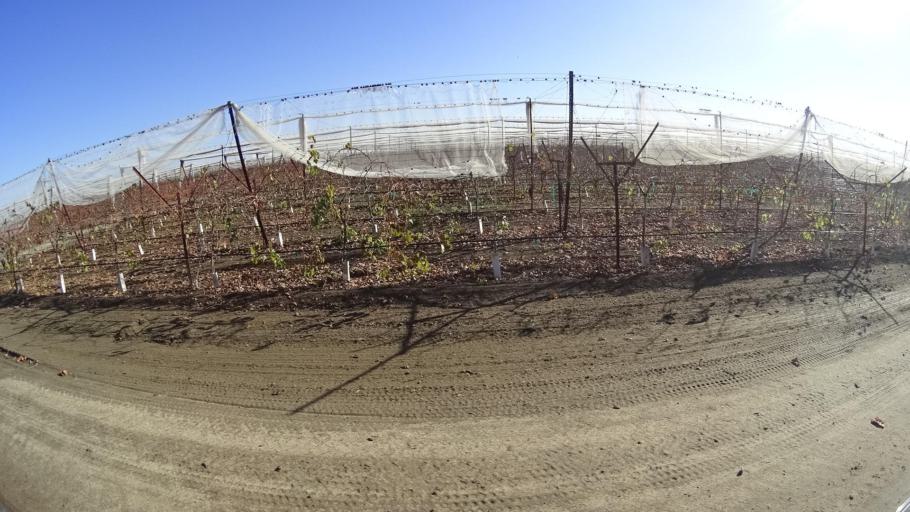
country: US
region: California
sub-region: Kern County
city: McFarland
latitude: 35.6975
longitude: -119.2675
